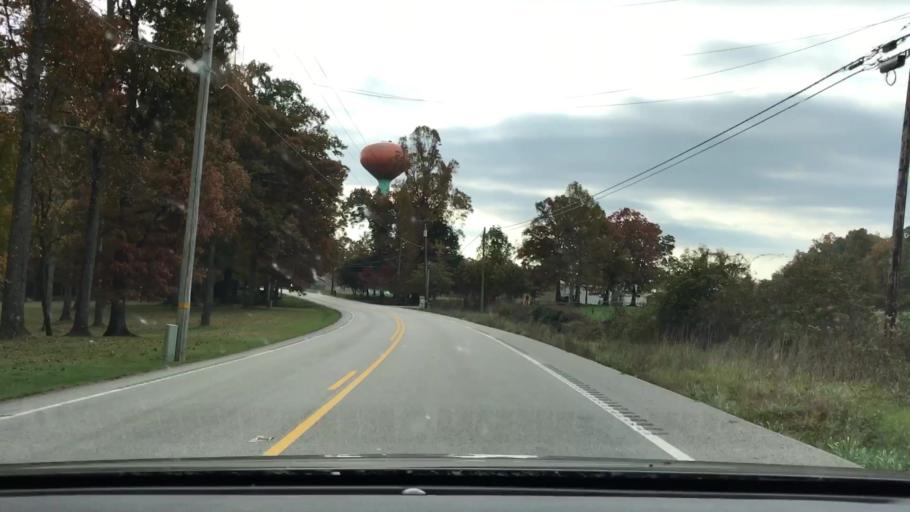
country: US
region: Tennessee
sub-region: Fentress County
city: Jamestown
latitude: 36.3759
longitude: -84.8734
